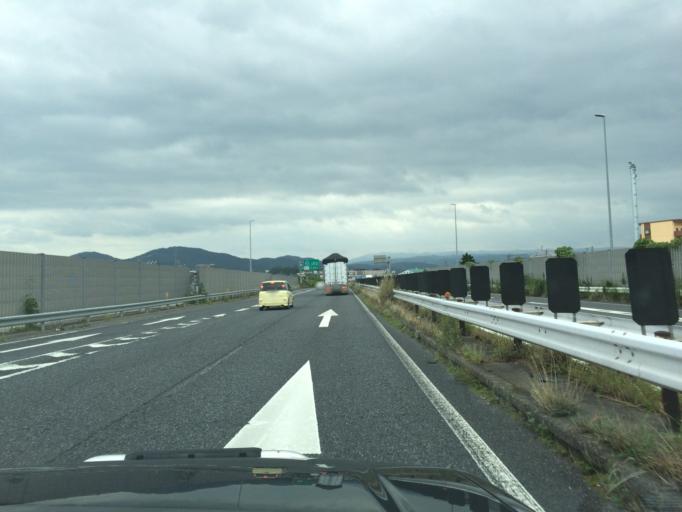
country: JP
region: Mie
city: Ueno-ebisumachi
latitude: 34.7530
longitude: 136.1347
